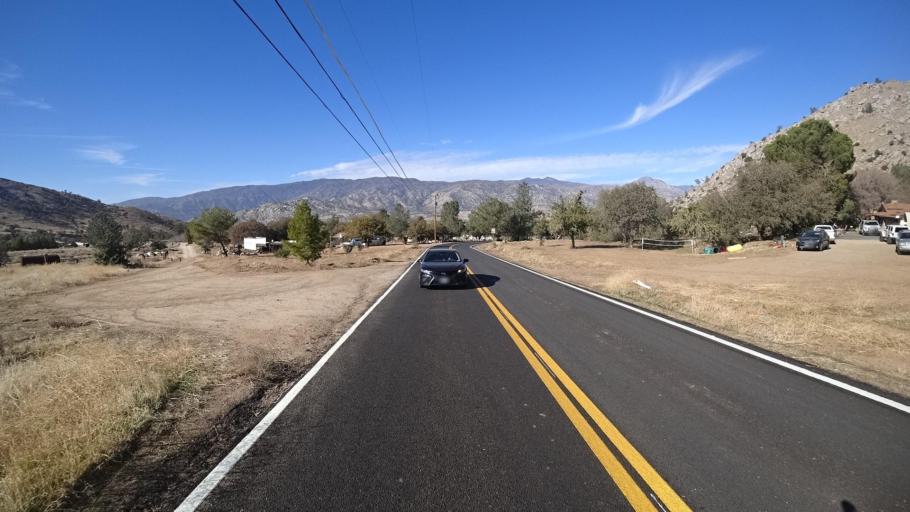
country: US
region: California
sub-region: Kern County
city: Lake Isabella
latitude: 35.6019
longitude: -118.4602
